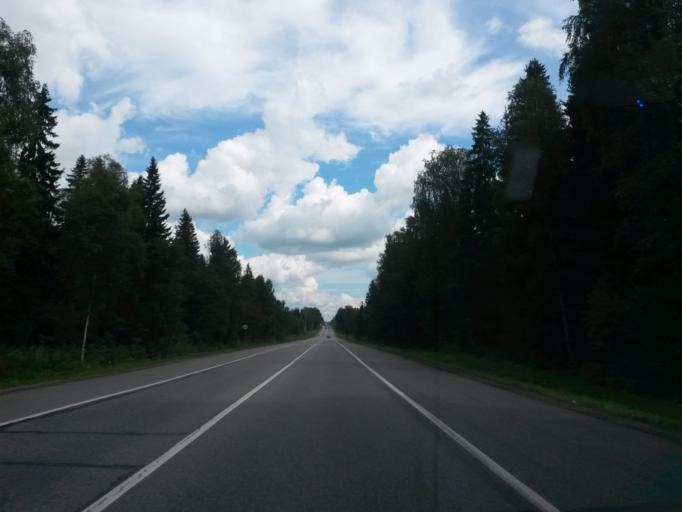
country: RU
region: Jaroslavl
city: Pereslavl'-Zalesskiy
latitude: 56.6379
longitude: 38.6794
